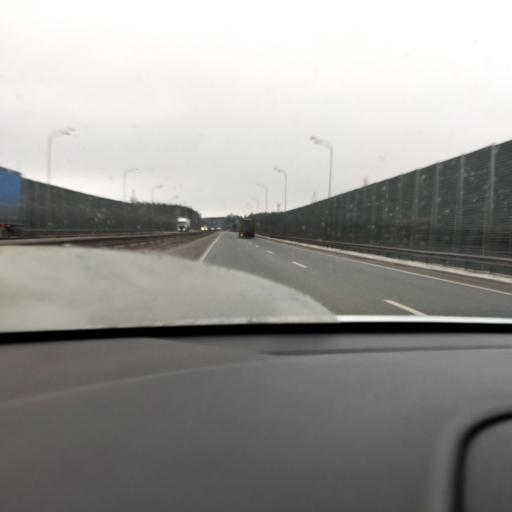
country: RU
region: Tatarstan
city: Osinovo
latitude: 55.8216
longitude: 48.8449
